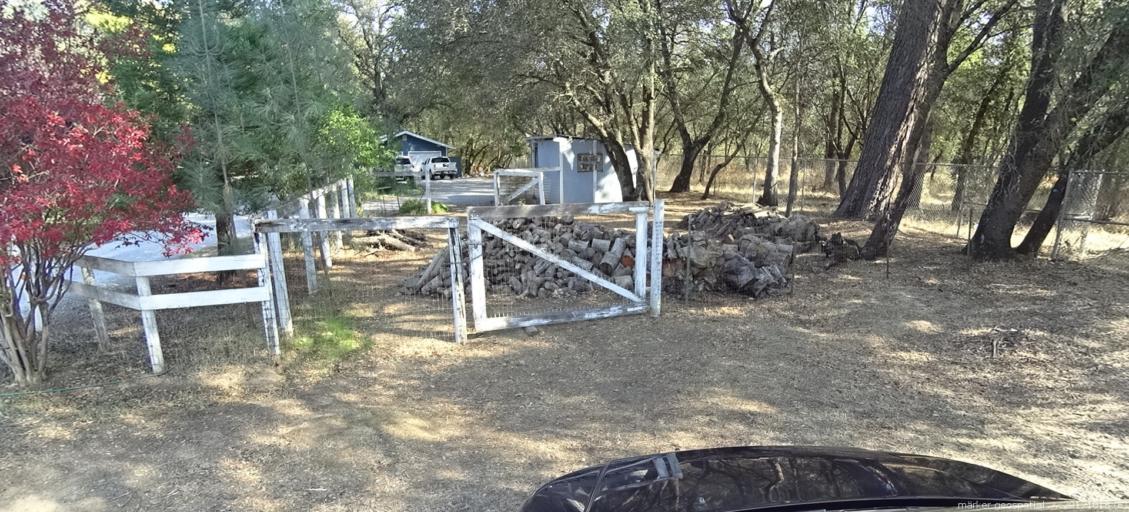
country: US
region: California
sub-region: Shasta County
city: Palo Cedro
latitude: 40.5711
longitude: -122.2284
